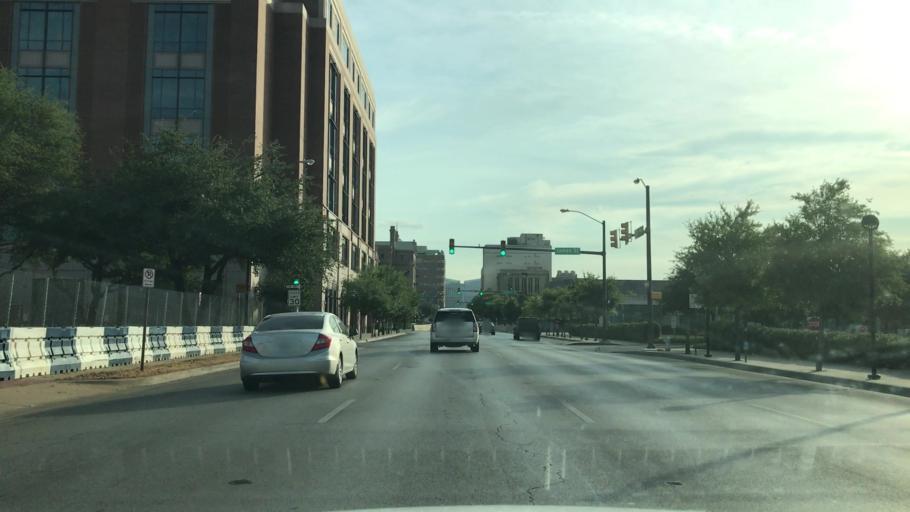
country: US
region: Texas
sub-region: Tarrant County
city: Fort Worth
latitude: 32.7591
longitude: -97.3307
